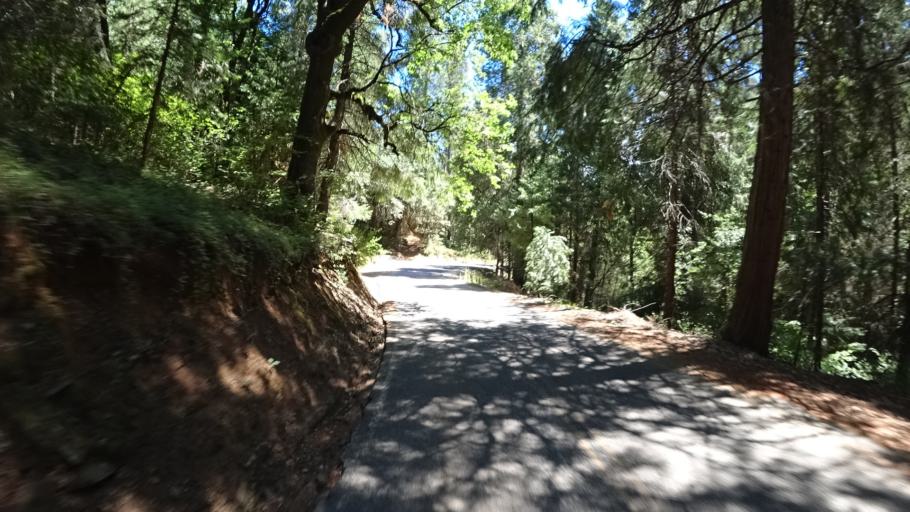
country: US
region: California
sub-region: Amador County
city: Pioneer
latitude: 38.3504
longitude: -120.5469
